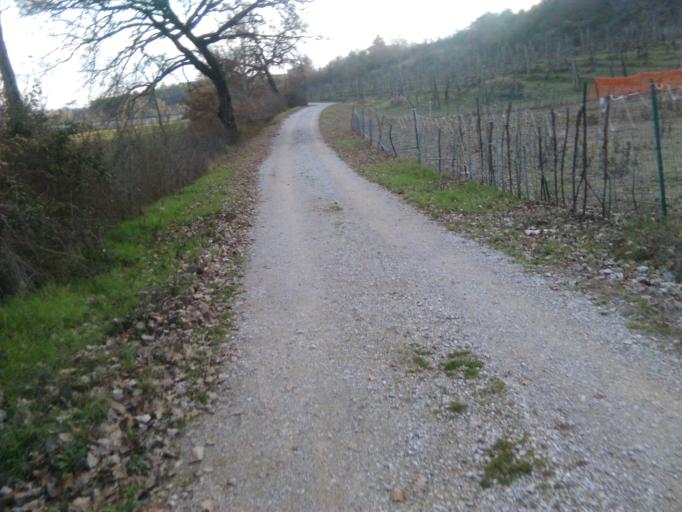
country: IT
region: Umbria
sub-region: Provincia di Perugia
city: Lacugnano
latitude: 43.0888
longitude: 12.3571
